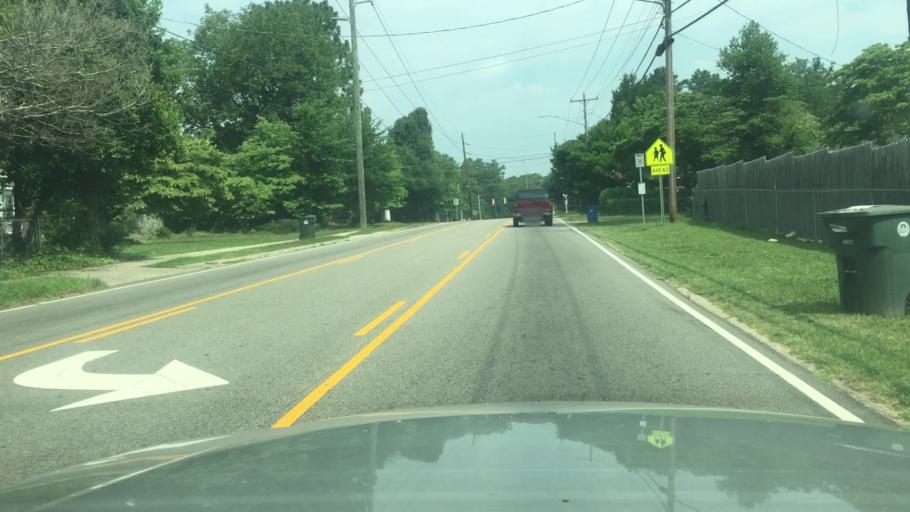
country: US
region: North Carolina
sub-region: Cumberland County
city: Hope Mills
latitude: 35.0289
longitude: -78.9447
